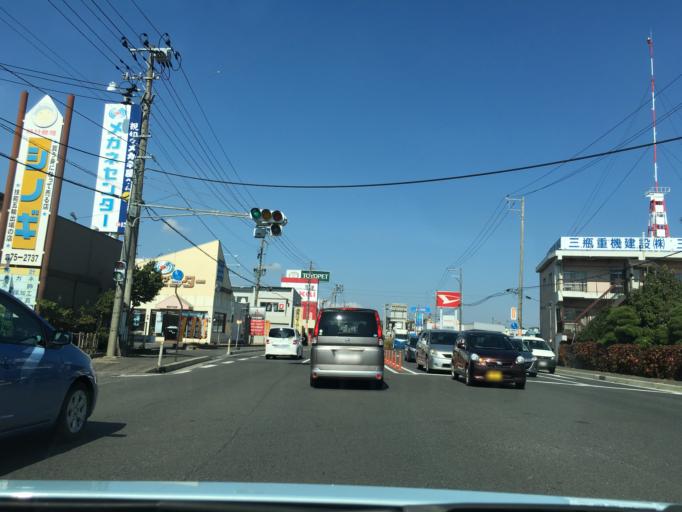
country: JP
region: Fukushima
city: Sukagawa
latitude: 37.3013
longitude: 140.3674
